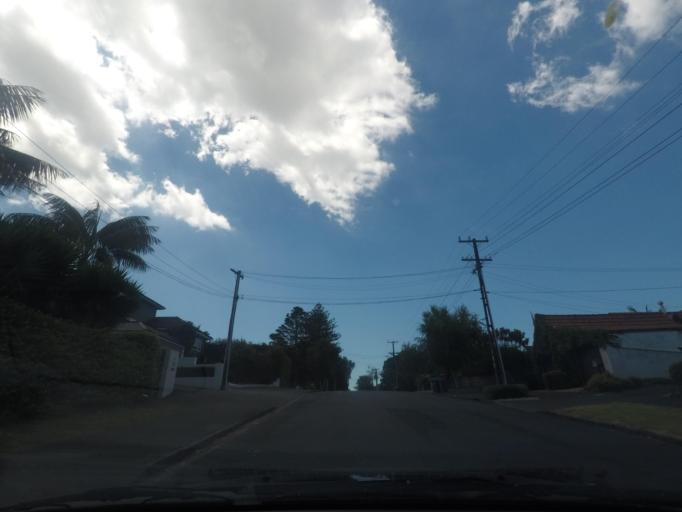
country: NZ
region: Auckland
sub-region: Auckland
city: Auckland
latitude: -36.8882
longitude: 174.7670
